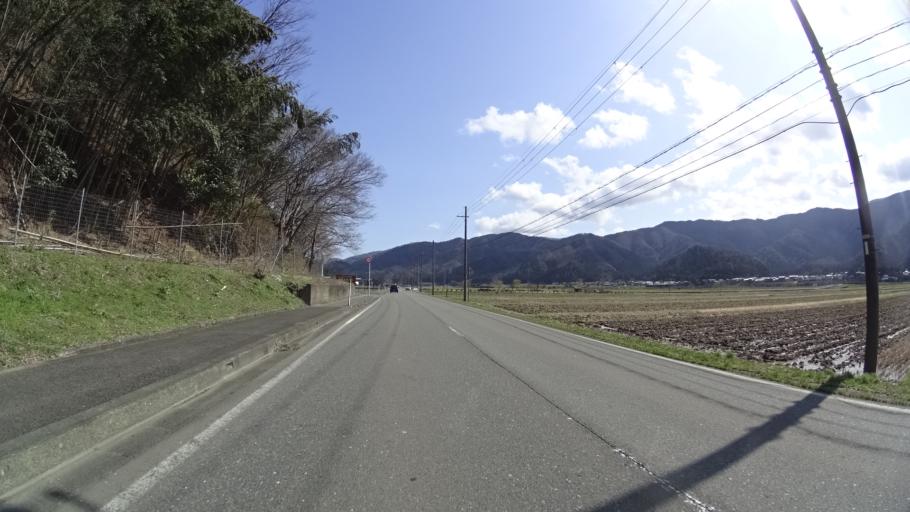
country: JP
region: Fukui
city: Obama
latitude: 35.4636
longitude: 135.8713
